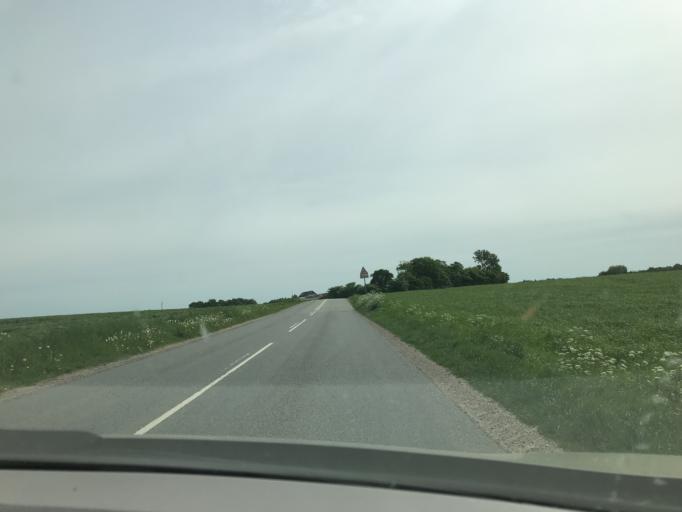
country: DK
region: Central Jutland
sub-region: Norddjurs Kommune
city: Allingabro
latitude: 56.5423
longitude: 10.3007
